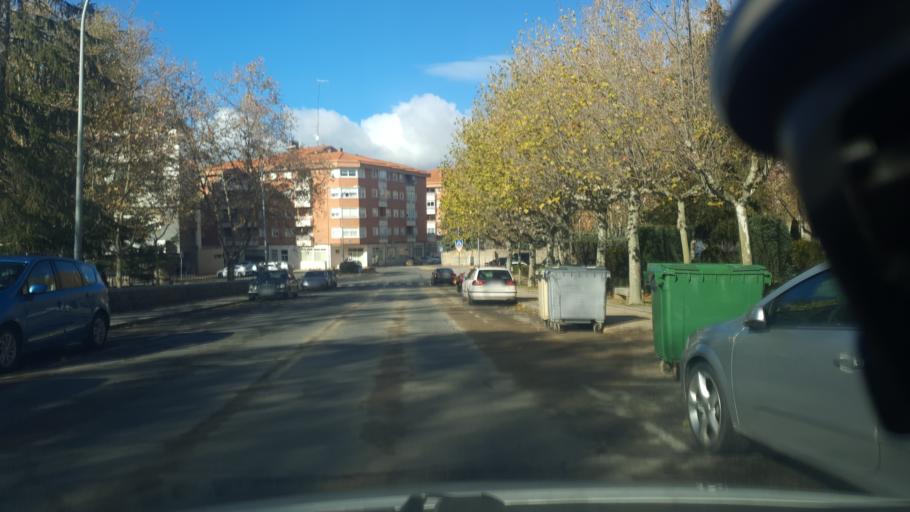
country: ES
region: Castille and Leon
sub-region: Provincia de Avila
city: Avila
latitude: 40.6589
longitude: -4.6851
